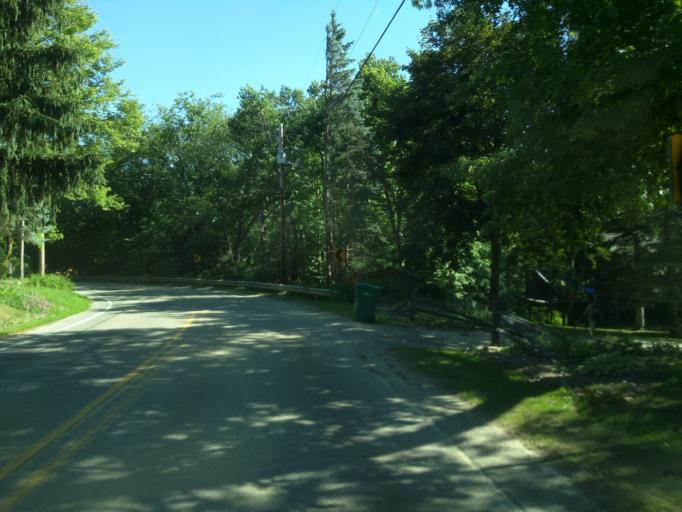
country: US
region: Michigan
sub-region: Eaton County
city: Waverly
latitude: 42.7690
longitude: -84.6600
